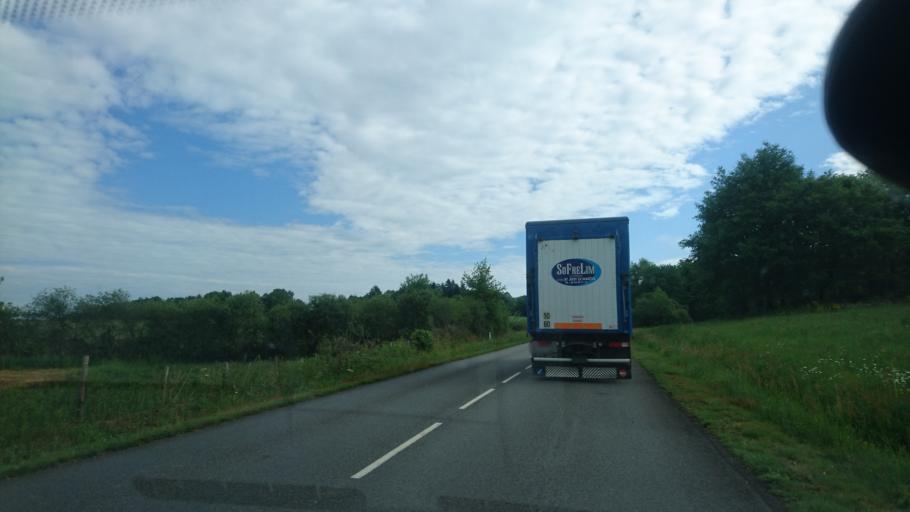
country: FR
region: Limousin
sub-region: Departement de la Haute-Vienne
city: Eymoutiers
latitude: 45.7642
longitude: 1.7498
